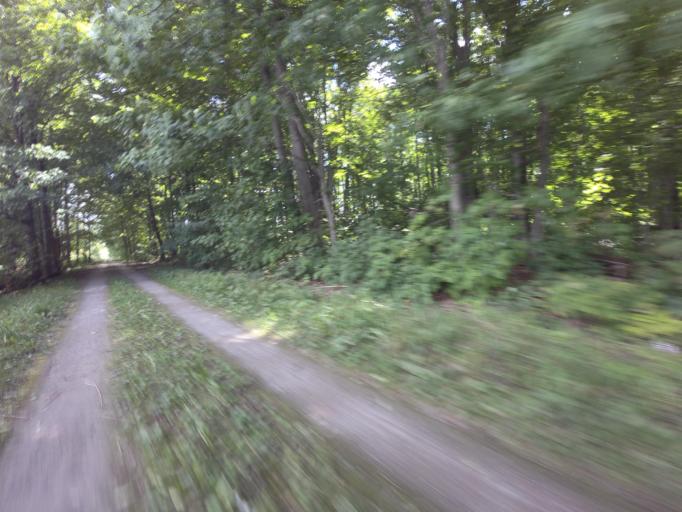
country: CA
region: Ontario
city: Orangeville
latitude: 43.7888
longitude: -80.2512
